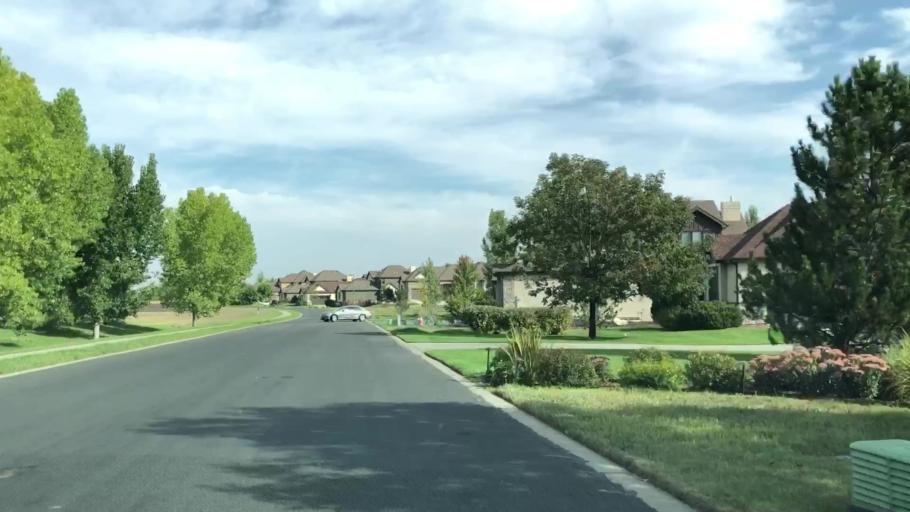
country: US
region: Colorado
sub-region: Larimer County
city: Loveland
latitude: 40.4317
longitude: -105.0515
